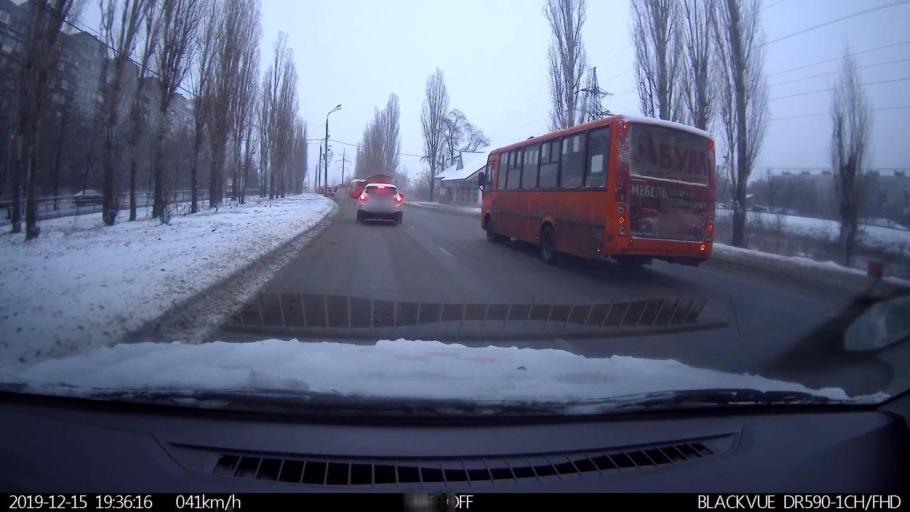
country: RU
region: Nizjnij Novgorod
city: Nizhniy Novgorod
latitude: 56.3335
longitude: 43.9313
